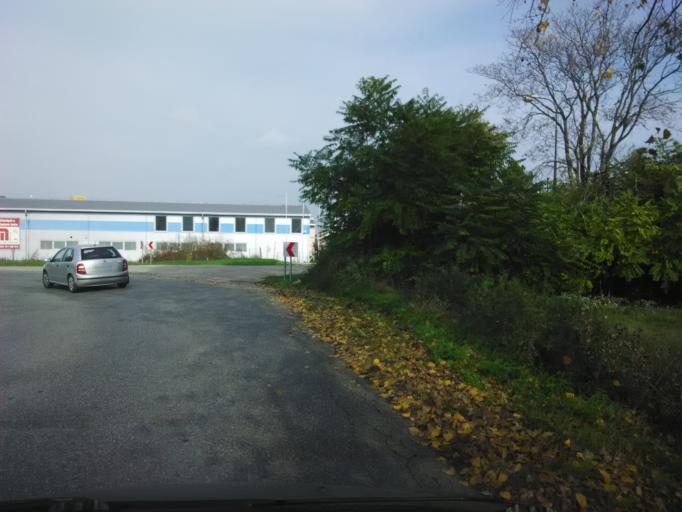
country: SK
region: Nitriansky
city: Komarno
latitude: 47.7622
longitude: 18.0961
